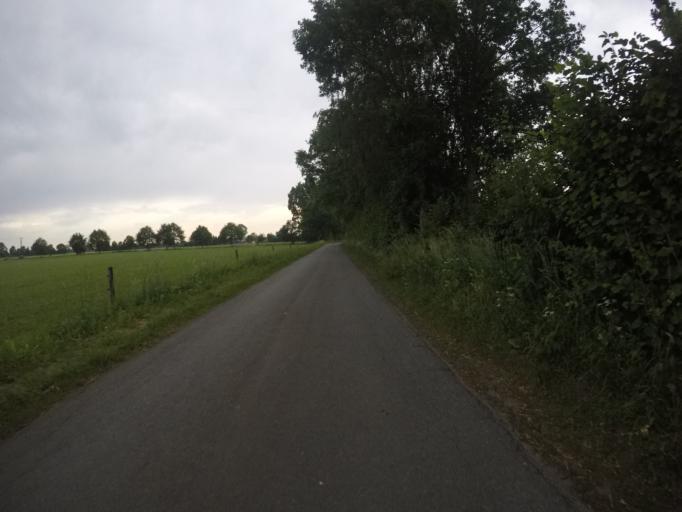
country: DE
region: North Rhine-Westphalia
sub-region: Regierungsbezirk Munster
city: Isselburg
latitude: 51.8360
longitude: 6.5396
